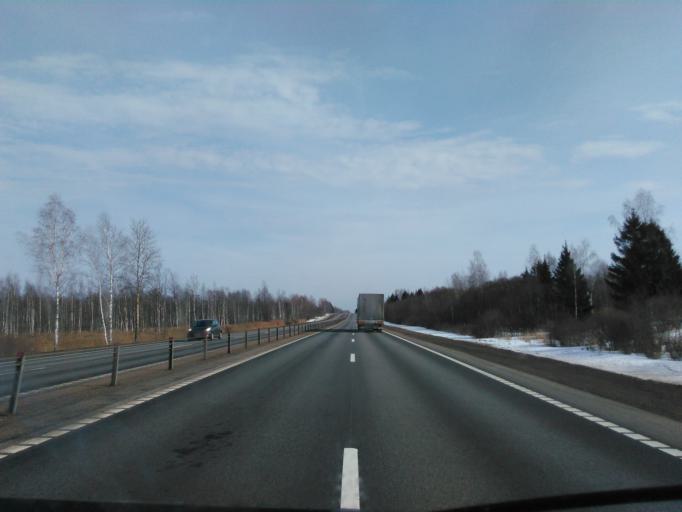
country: BY
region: Vitebsk
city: Dubrowna
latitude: 54.6896
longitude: 30.9094
